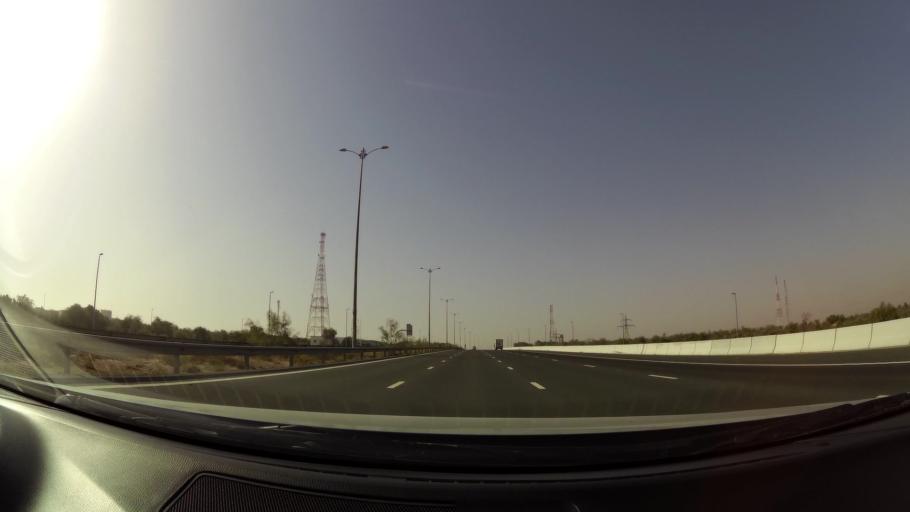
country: OM
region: Al Buraimi
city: Al Buraymi
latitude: 24.5818
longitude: 55.7426
